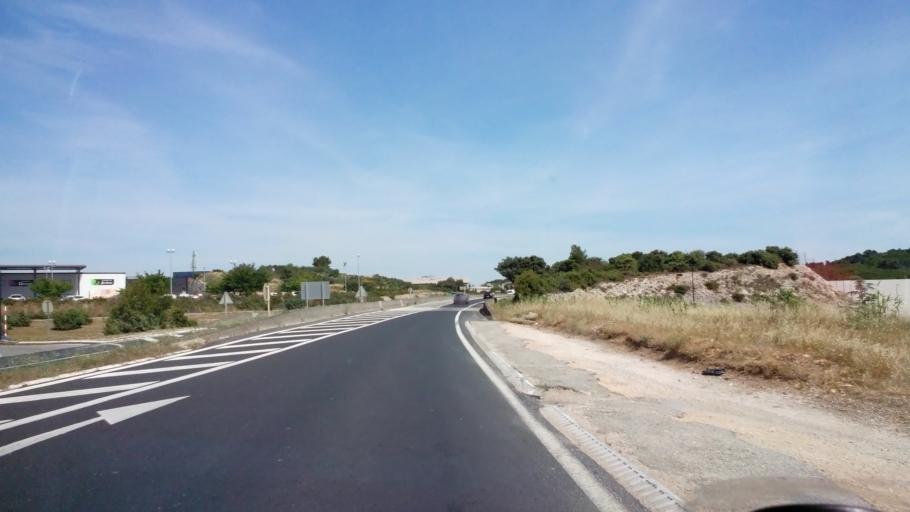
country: FR
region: Languedoc-Roussillon
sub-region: Departement du Gard
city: Les Angles
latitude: 43.9597
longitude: 4.7460
